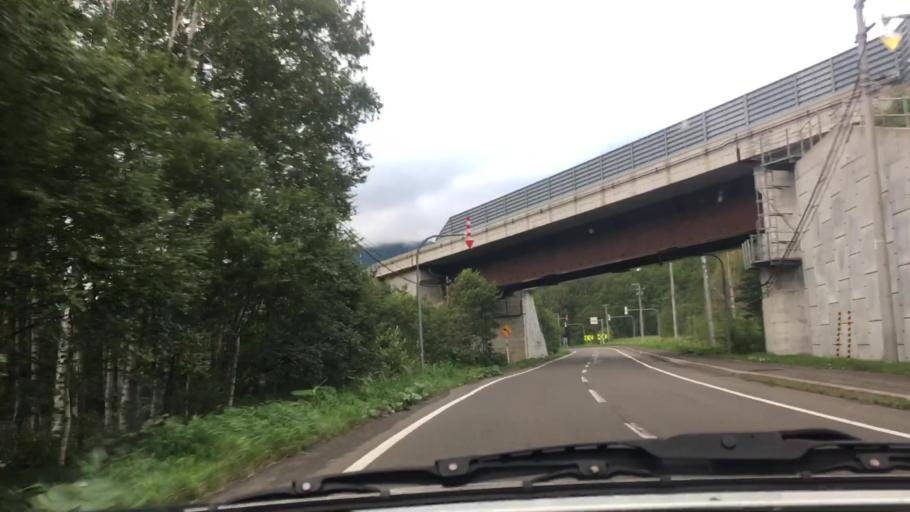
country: JP
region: Hokkaido
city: Shimo-furano
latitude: 43.0522
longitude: 142.6443
